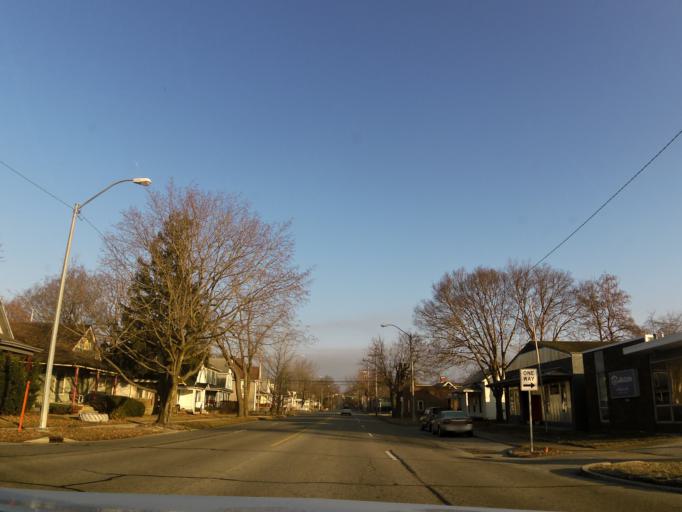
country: US
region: Indiana
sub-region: Bartholomew County
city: Columbus
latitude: 39.2124
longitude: -85.9214
